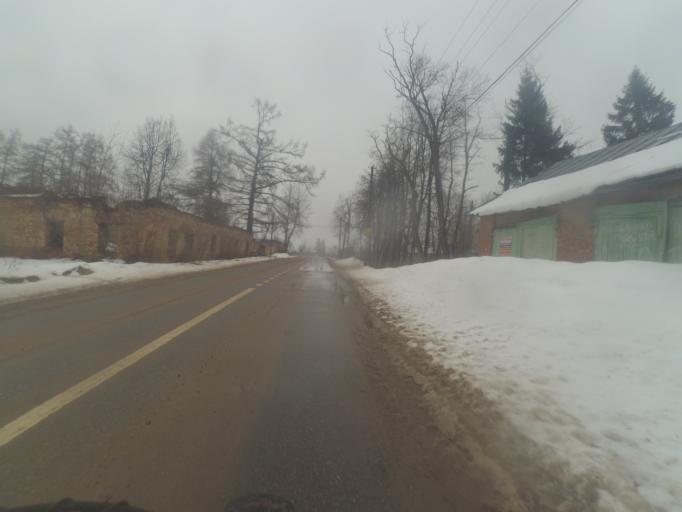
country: RU
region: Moskovskaya
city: Avtopoligon
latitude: 56.2597
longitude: 37.2482
